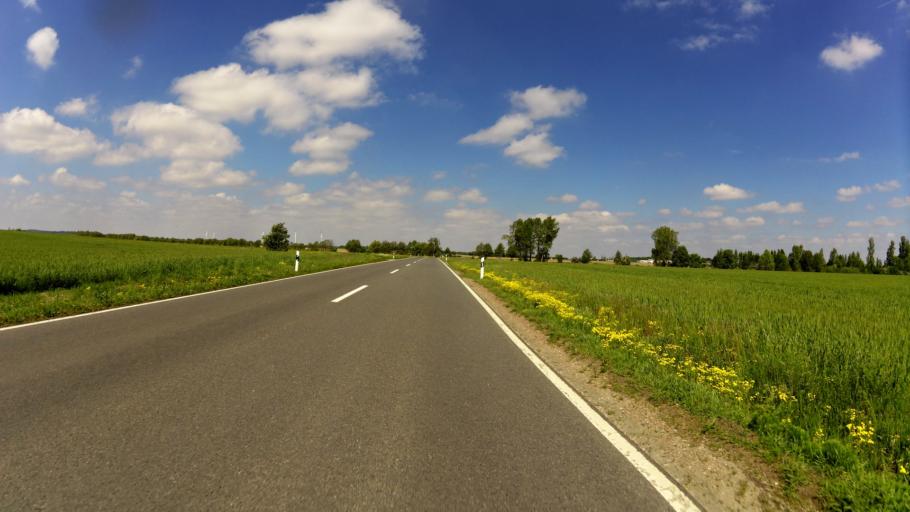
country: DE
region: Saxony
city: Belgern
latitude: 51.4556
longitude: 13.1596
